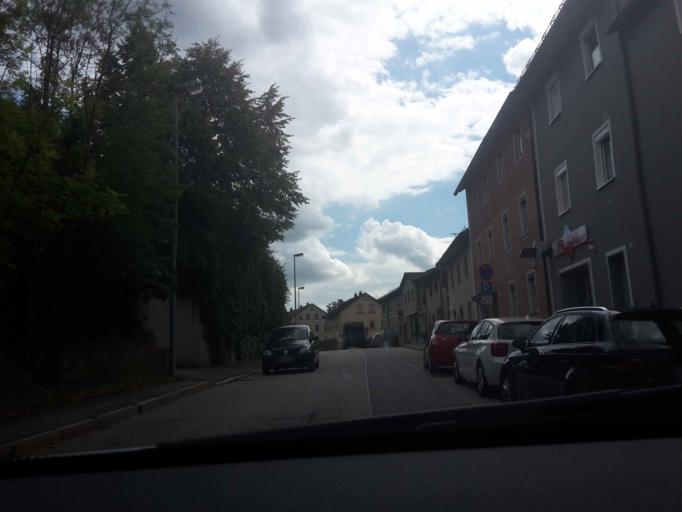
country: DE
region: Bavaria
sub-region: Lower Bavaria
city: Zwiesel
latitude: 49.0186
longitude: 13.2314
